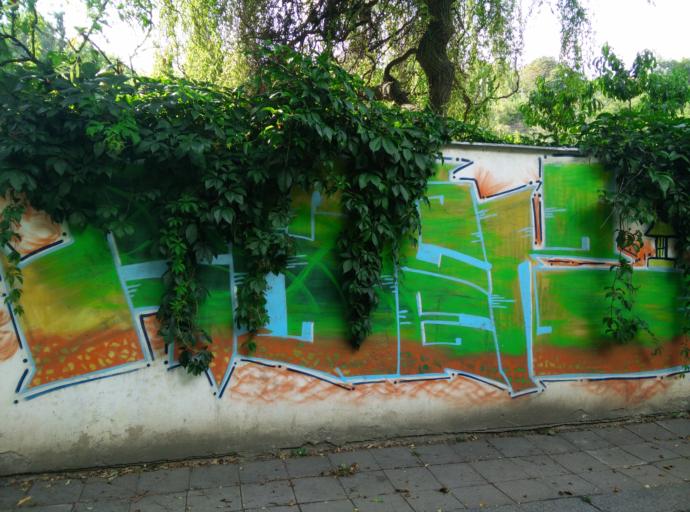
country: CZ
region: South Moravian
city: Bilovice nad Svitavou
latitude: 49.2253
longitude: 16.6372
